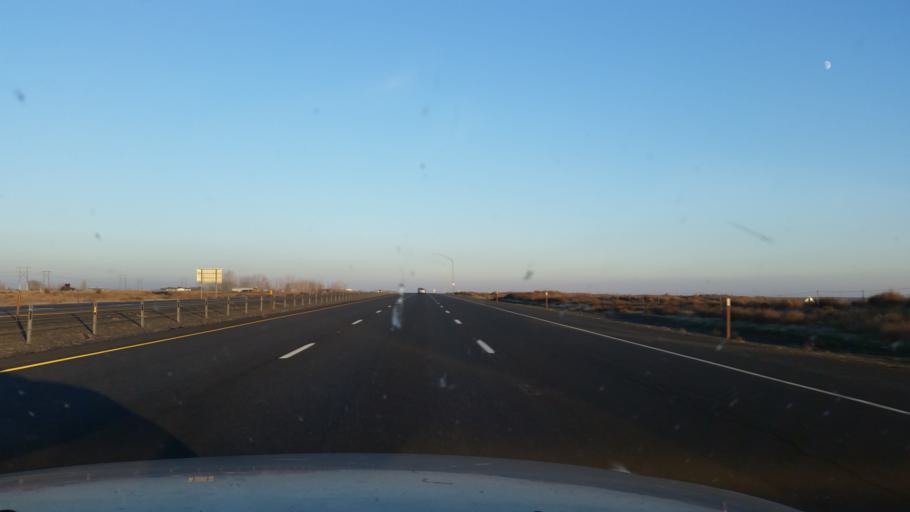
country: US
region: Washington
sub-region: Grant County
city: Cascade Valley
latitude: 47.1040
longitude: -119.4448
